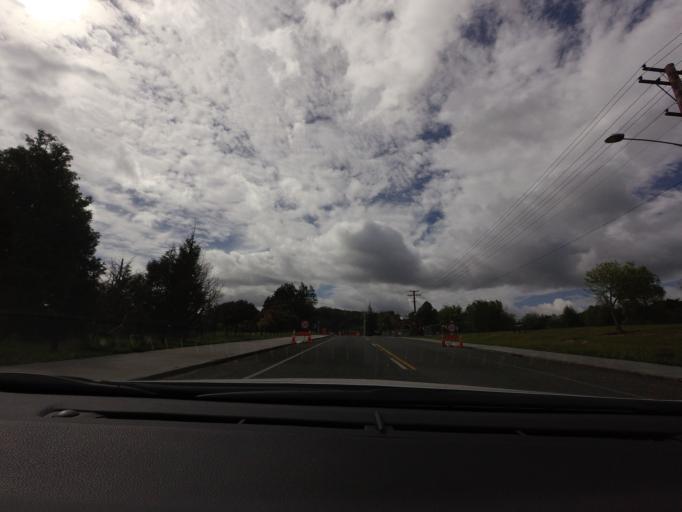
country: NZ
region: Bay of Plenty
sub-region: Rotorua District
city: Rotorua
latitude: -38.1618
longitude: 176.2431
